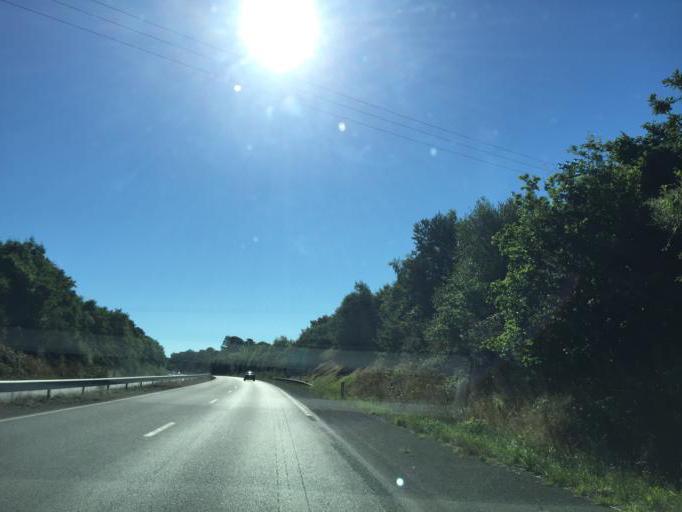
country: FR
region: Brittany
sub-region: Departement des Cotes-d'Armor
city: Plelan-le-Petit
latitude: 48.4247
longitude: -2.2150
